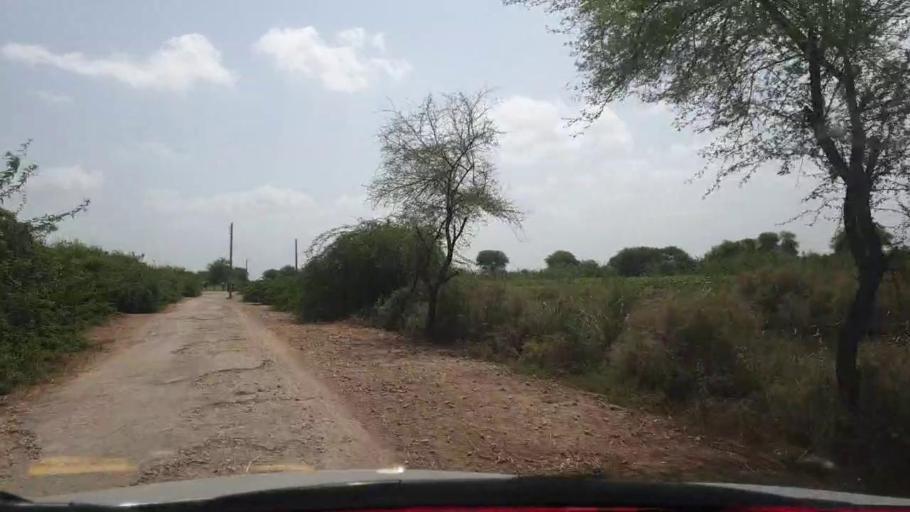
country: PK
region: Sindh
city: Talhar
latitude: 24.8911
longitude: 68.9063
